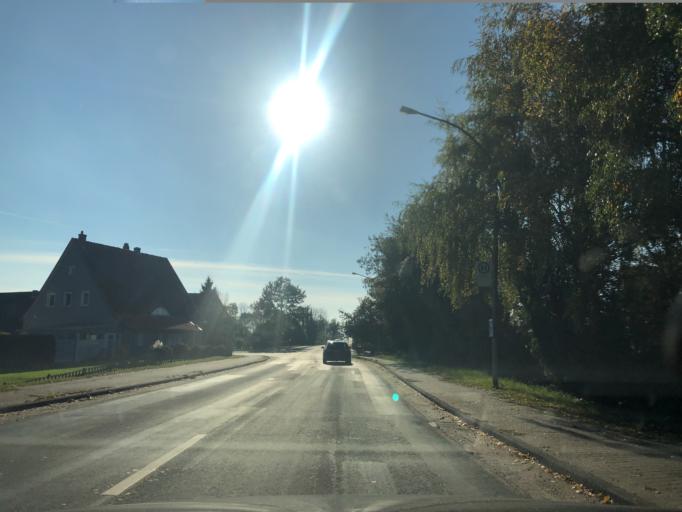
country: DE
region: Lower Saxony
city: Lemwerder
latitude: 53.1781
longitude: 8.5575
